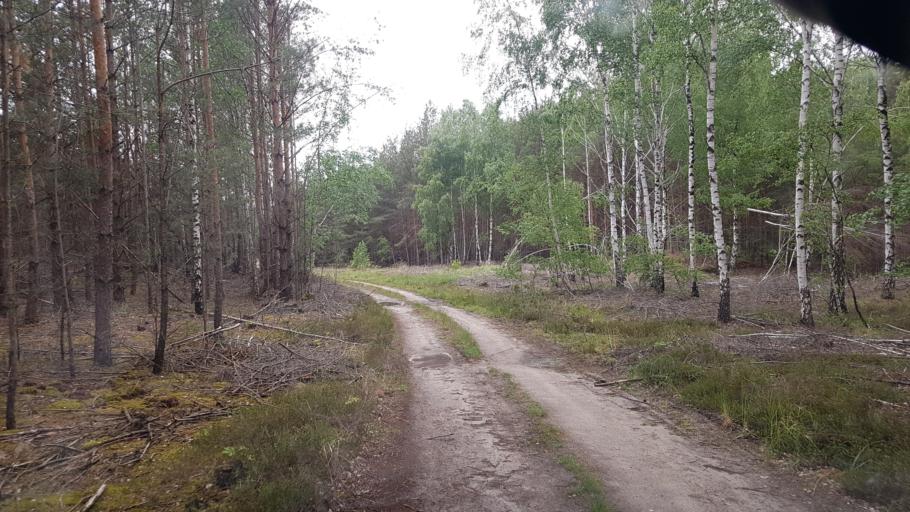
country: DE
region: Brandenburg
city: Ruckersdorf
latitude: 51.5477
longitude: 13.5285
